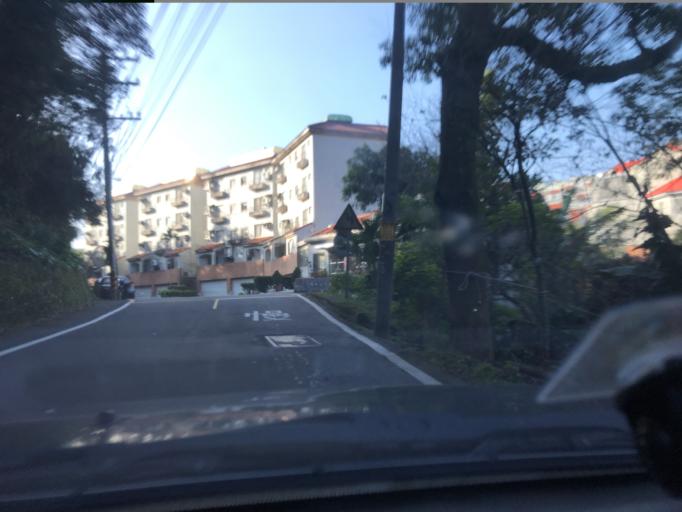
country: TW
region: Taiwan
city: Daxi
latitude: 24.8415
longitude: 121.2152
